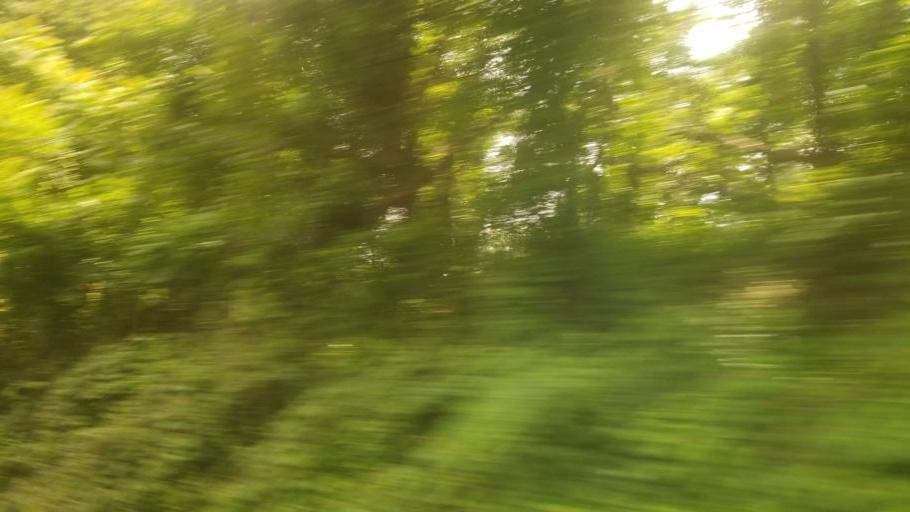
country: US
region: Maryland
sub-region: Montgomery County
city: Poolesville
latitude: 39.2200
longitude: -77.4159
